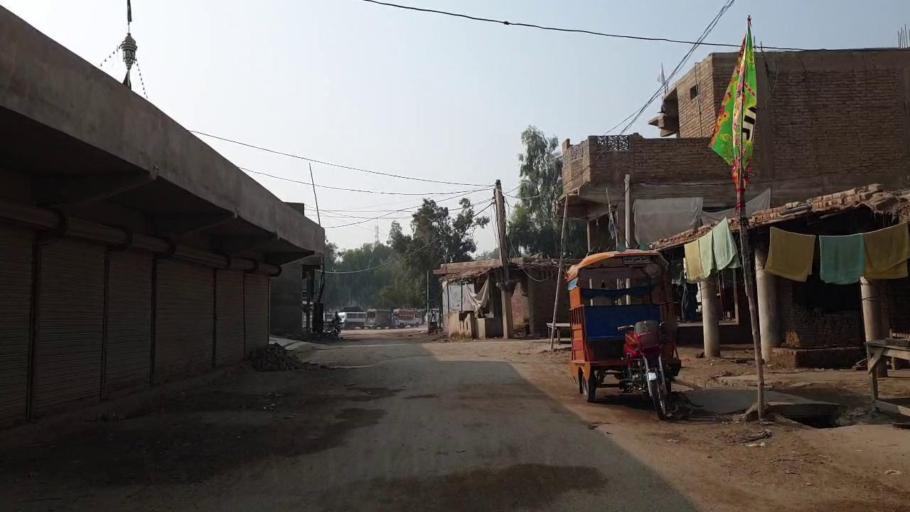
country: PK
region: Sindh
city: Sehwan
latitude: 26.4279
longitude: 67.8559
